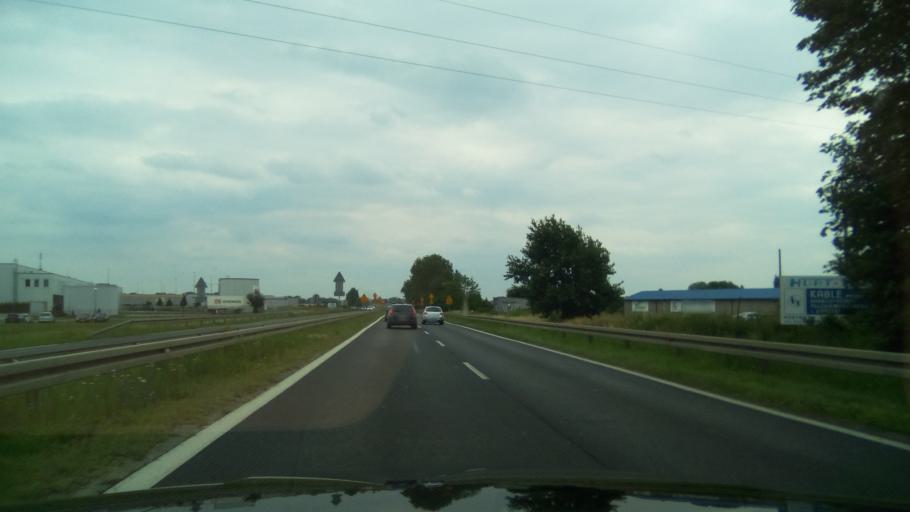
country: PL
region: Greater Poland Voivodeship
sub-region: Powiat poznanski
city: Kostrzyn
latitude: 52.4003
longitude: 17.2361
